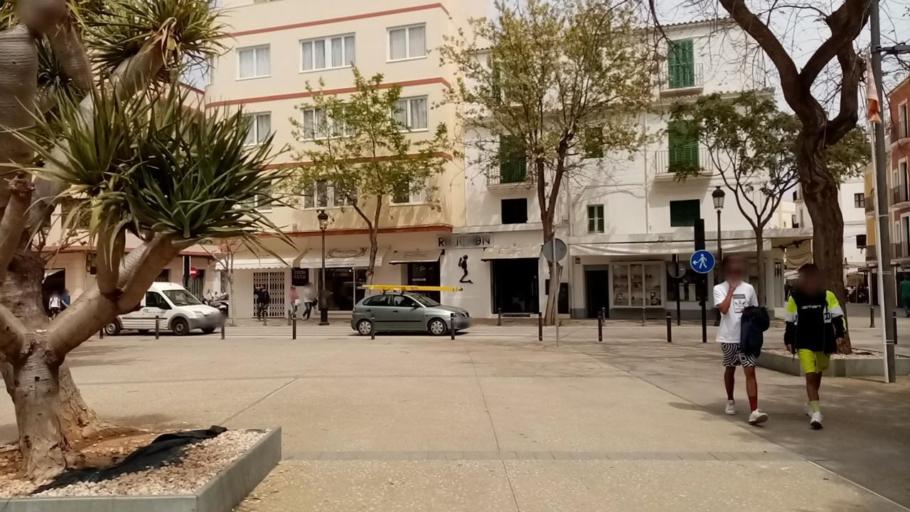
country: ES
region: Balearic Islands
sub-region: Illes Balears
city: Ibiza
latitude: 38.9097
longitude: 1.4347
